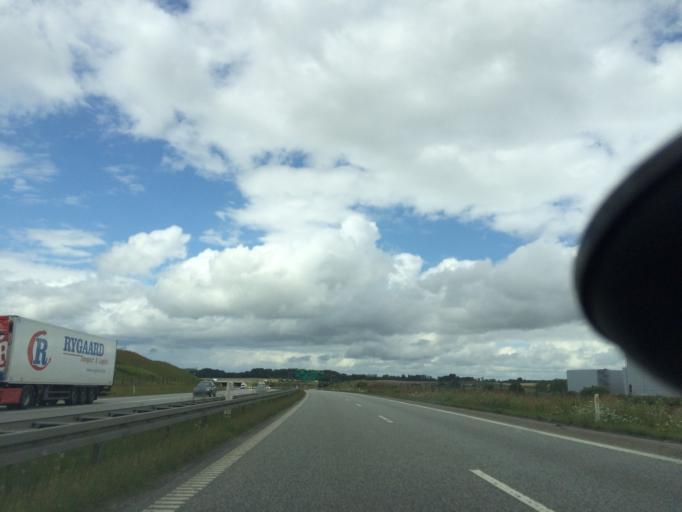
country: DK
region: Central Jutland
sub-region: Arhus Kommune
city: Framlev
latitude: 56.1581
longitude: 10.0587
